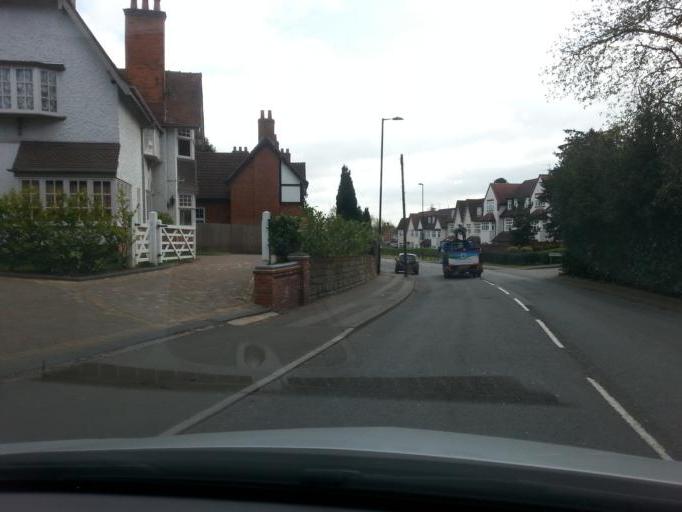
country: GB
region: England
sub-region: City and Borough of Birmingham
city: Sutton Coldfield
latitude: 52.5865
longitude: -1.8354
